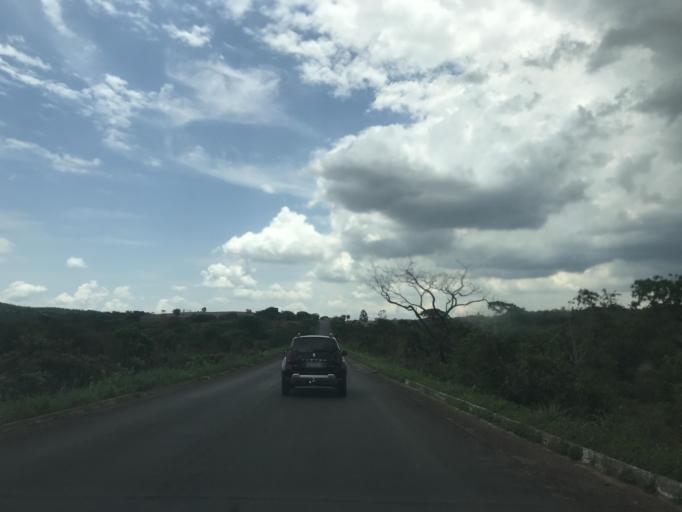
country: BR
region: Goias
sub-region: Vianopolis
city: Vianopolis
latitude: -16.9473
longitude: -48.5796
